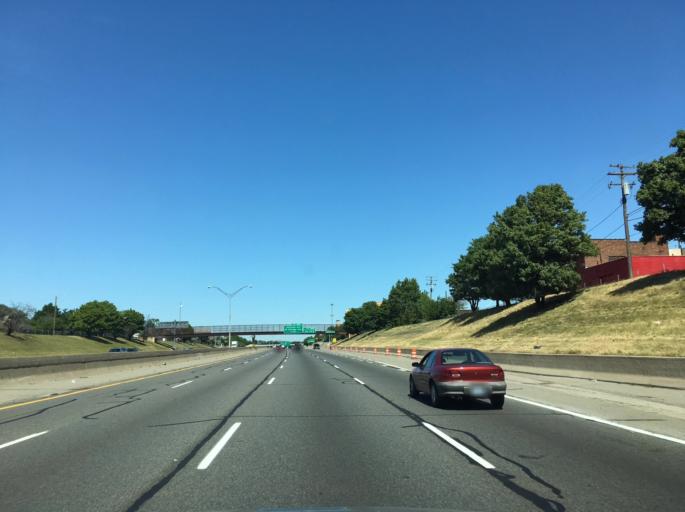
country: US
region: Michigan
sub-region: Wayne County
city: Highland Park
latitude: 42.3621
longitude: -83.1245
